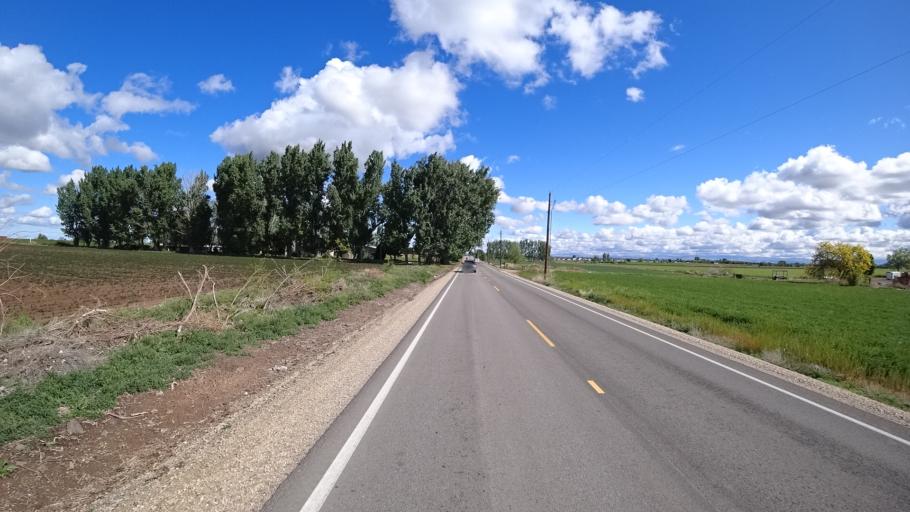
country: US
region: Idaho
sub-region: Ada County
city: Kuna
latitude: 43.4914
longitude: -116.4539
